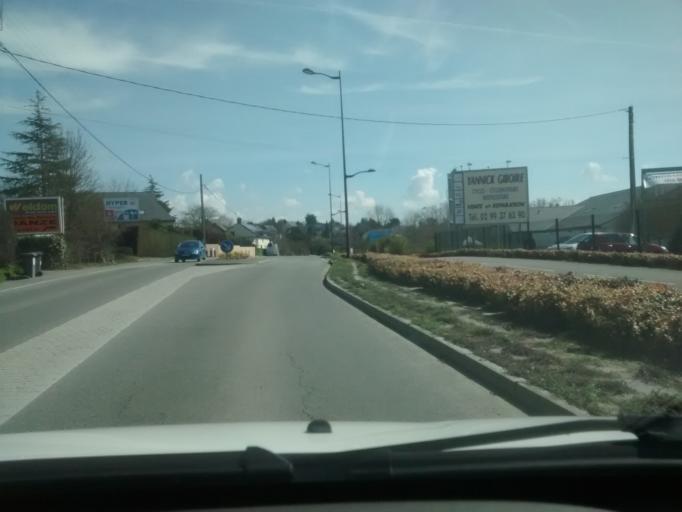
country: FR
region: Brittany
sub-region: Departement d'Ille-et-Vilaine
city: Chateaugiron
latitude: 48.0548
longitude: -1.5158
